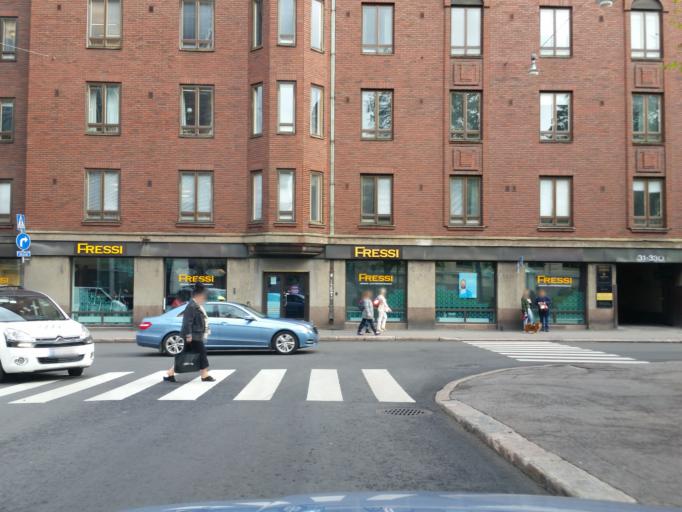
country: FI
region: Uusimaa
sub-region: Helsinki
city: Helsinki
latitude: 60.1682
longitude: 24.9347
